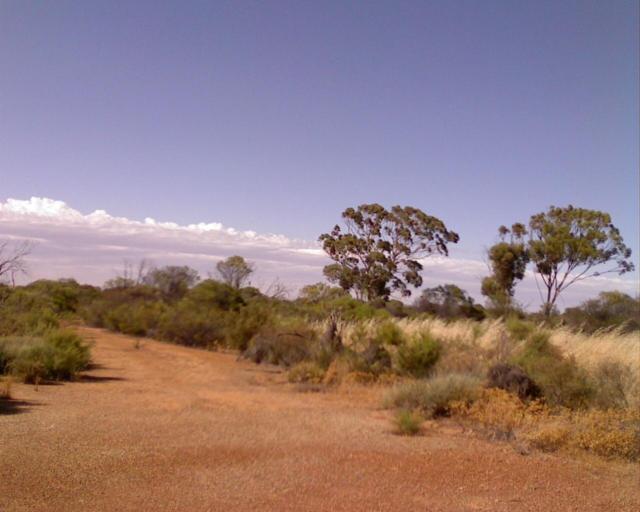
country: AU
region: Western Australia
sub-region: Moora
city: Moora
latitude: -29.8647
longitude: 116.1656
